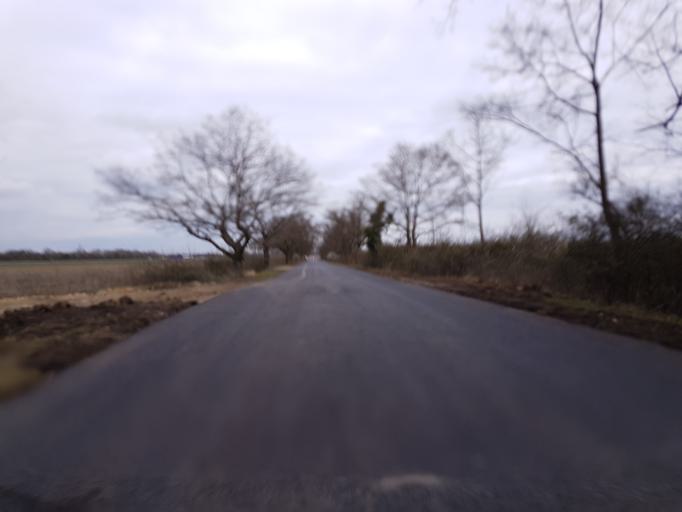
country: GB
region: England
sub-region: Cambridgeshire
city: Girton
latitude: 52.2348
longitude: 0.0540
